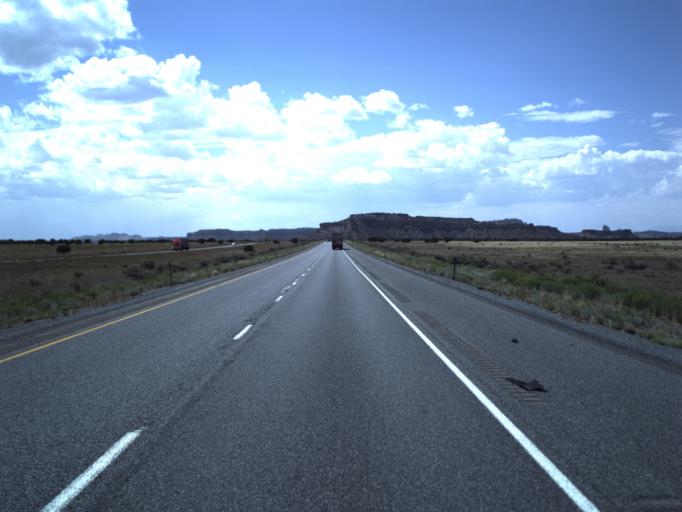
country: US
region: Utah
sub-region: Emery County
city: Castle Dale
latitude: 38.8931
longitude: -110.6282
